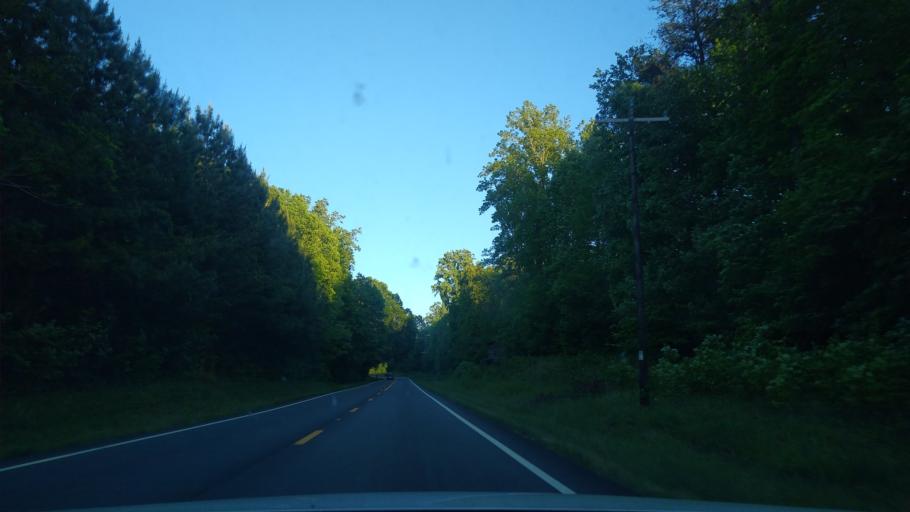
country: US
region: North Carolina
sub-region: Rockingham County
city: Reidsville
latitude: 36.3944
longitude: -79.5152
